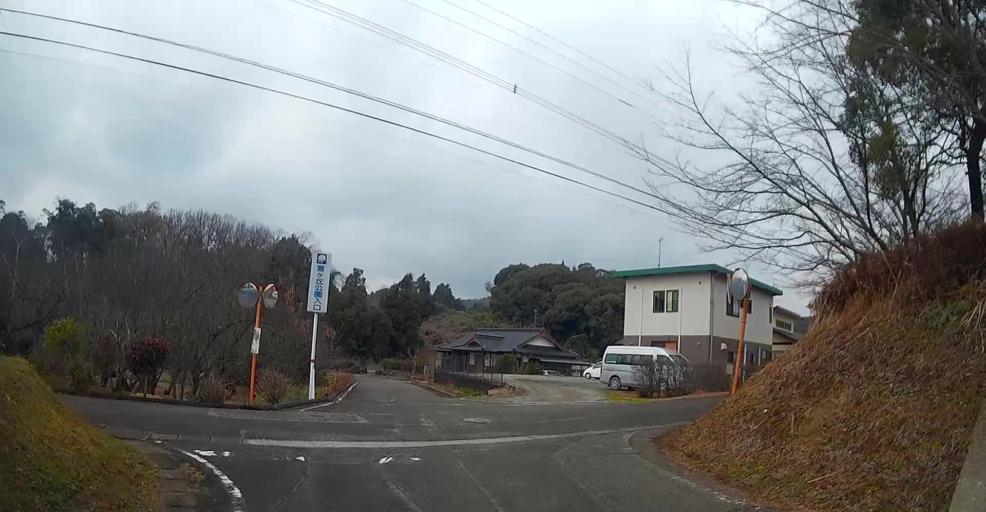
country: JP
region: Kumamoto
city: Matsubase
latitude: 32.6449
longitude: 130.7396
